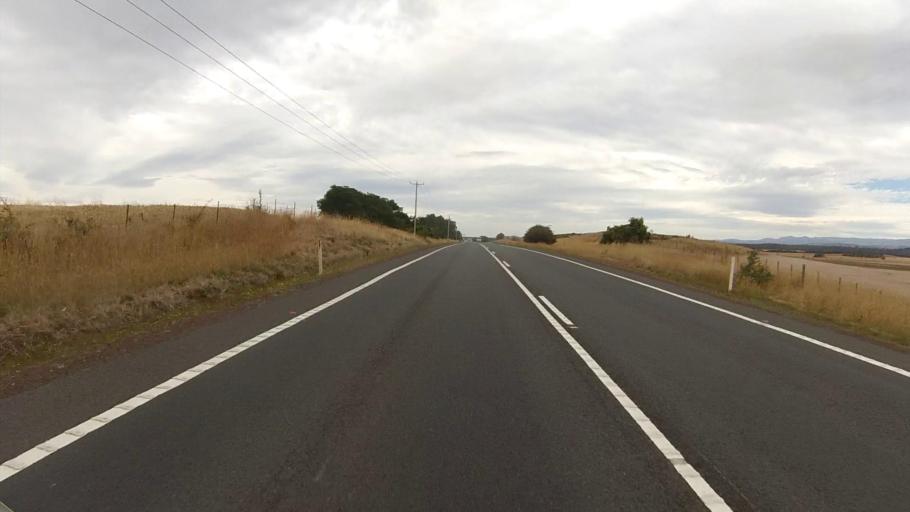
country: AU
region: Tasmania
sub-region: Northern Midlands
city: Evandale
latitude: -41.9069
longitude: 147.4795
